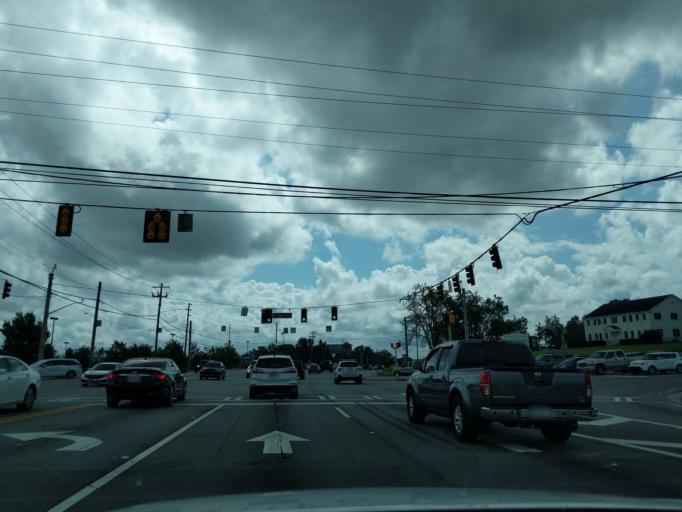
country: US
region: Georgia
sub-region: Columbia County
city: Evans
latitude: 33.5373
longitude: -82.1285
